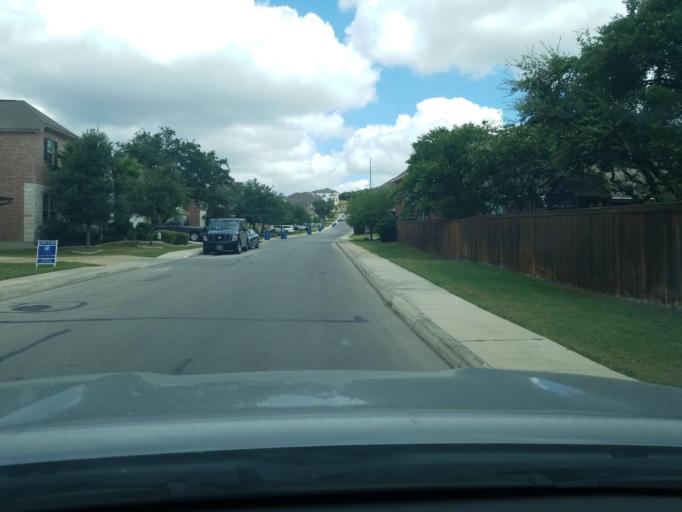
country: US
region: Texas
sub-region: Bexar County
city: Timberwood Park
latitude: 29.6636
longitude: -98.5115
